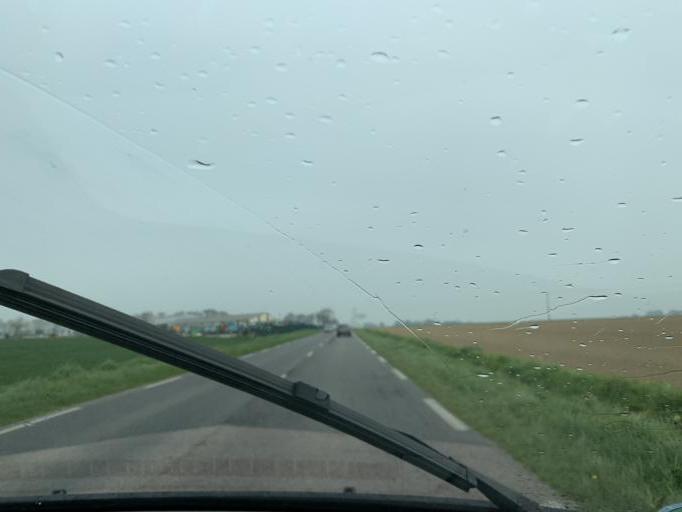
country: FR
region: Haute-Normandie
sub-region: Departement de la Seine-Maritime
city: Bertheauville
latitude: 49.7817
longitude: 0.5802
